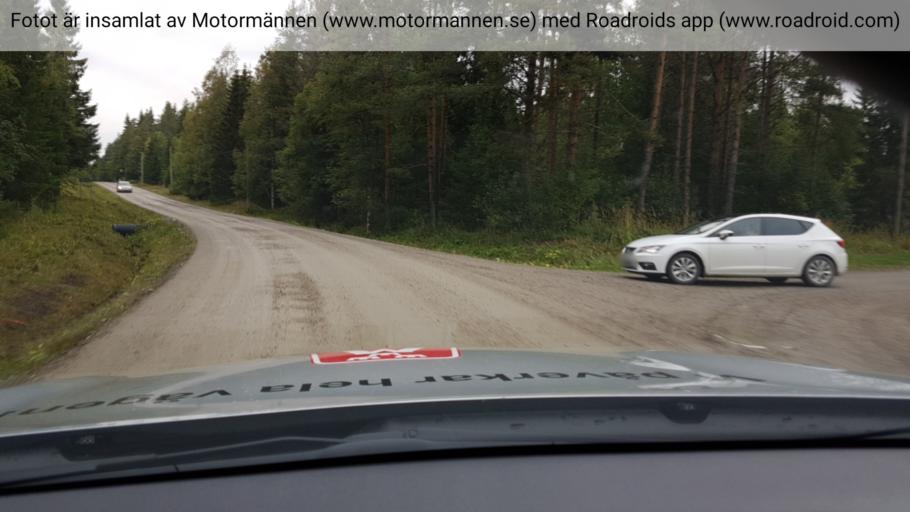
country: SE
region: Jaemtland
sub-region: Braecke Kommun
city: Braecke
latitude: 62.7776
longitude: 15.4781
